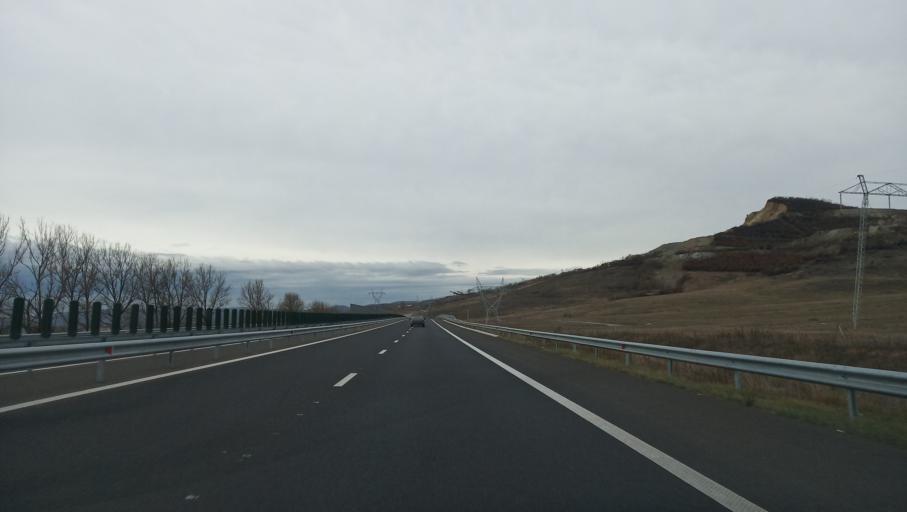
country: RO
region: Hunedoara
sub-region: Comuna Branisca
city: Branisca
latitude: 45.9427
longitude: 22.7298
